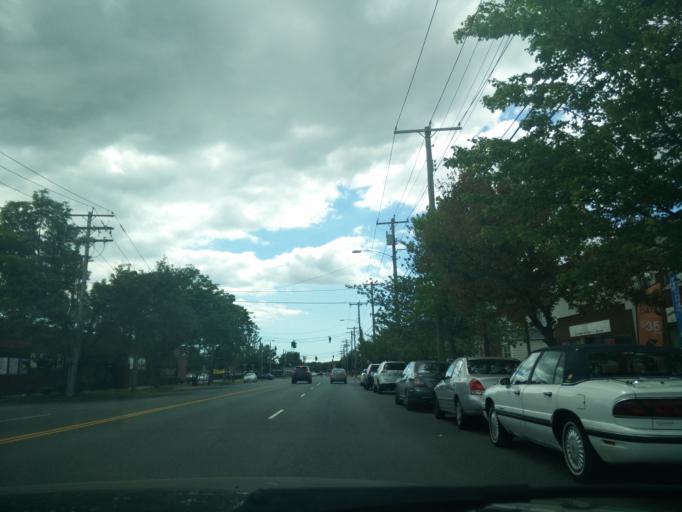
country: US
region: Connecticut
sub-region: New Haven County
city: New Haven
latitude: 41.3497
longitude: -72.9322
